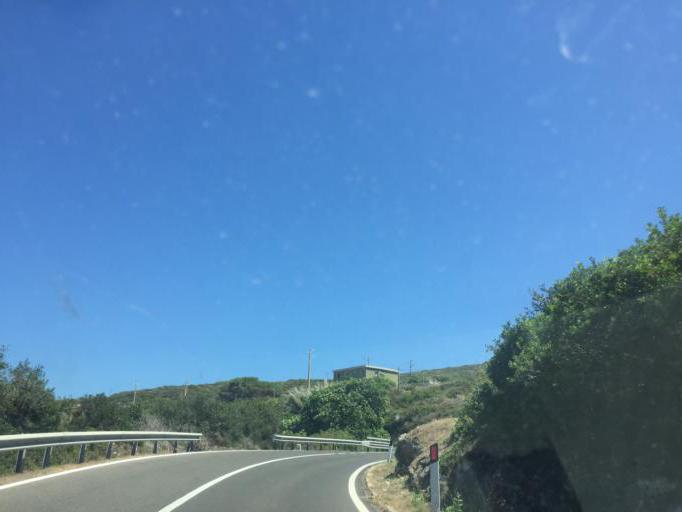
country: IT
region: Sardinia
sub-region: Provincia di Sassari
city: Castelsardo
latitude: 40.9103
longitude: 8.7303
